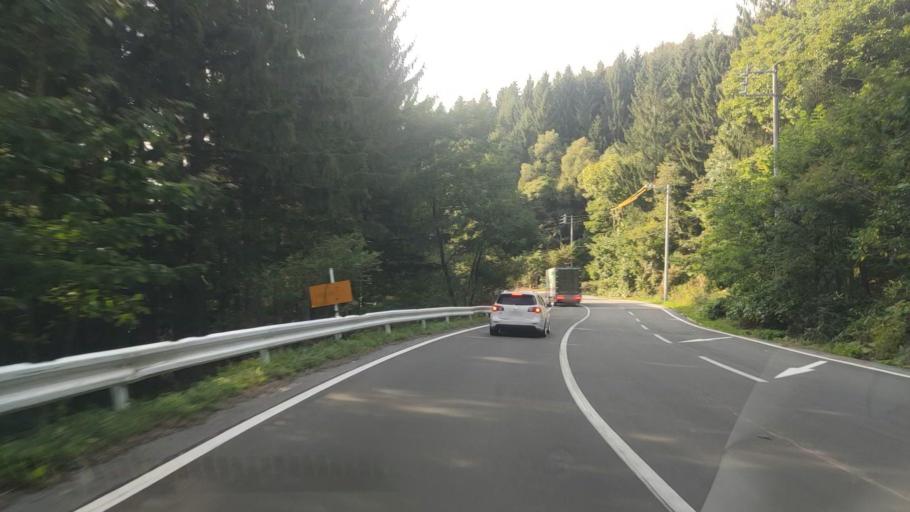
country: JP
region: Nagano
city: Ueda
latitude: 36.4929
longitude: 138.3937
